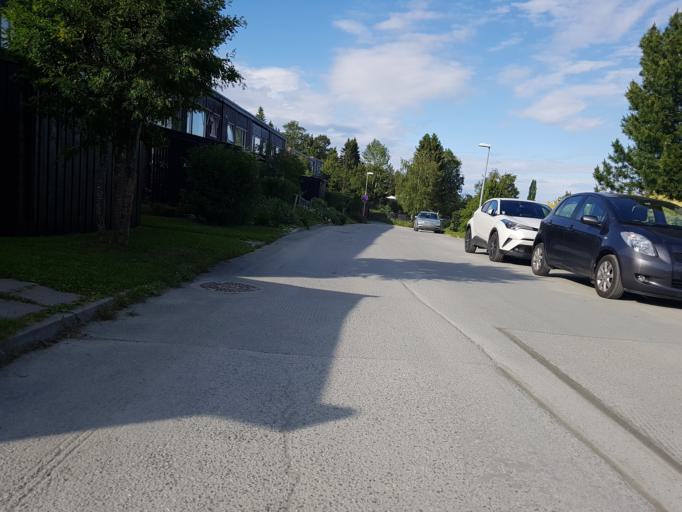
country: NO
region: Sor-Trondelag
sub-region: Trondheim
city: Trondheim
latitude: 63.4107
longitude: 10.3561
